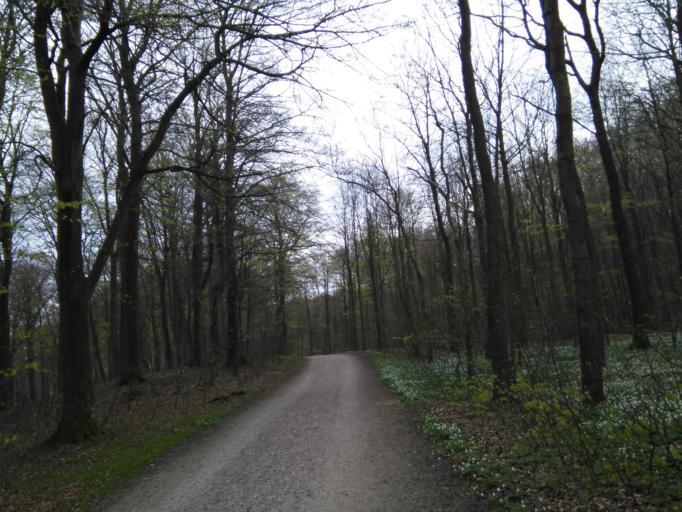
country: DK
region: Central Jutland
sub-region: Arhus Kommune
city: Beder
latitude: 56.0749
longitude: 10.2522
